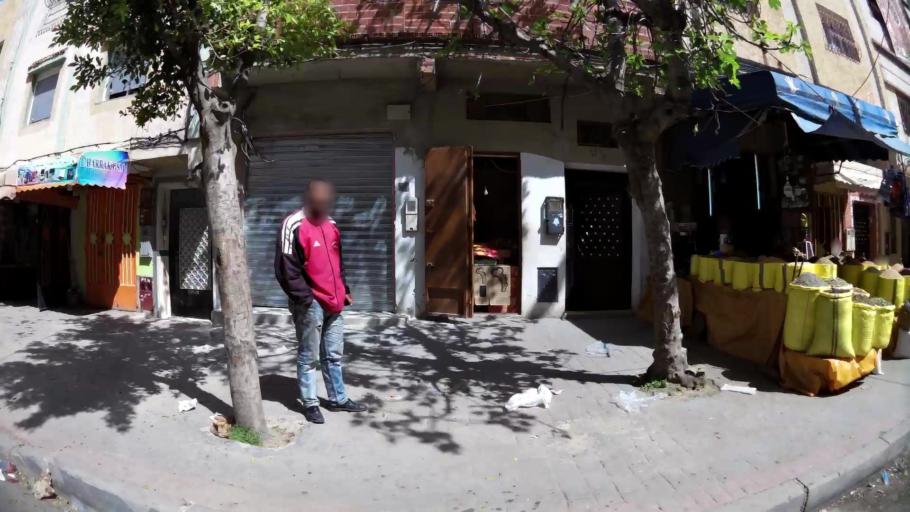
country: MA
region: Tanger-Tetouan
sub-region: Tanger-Assilah
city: Tangier
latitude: 35.7373
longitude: -5.8063
